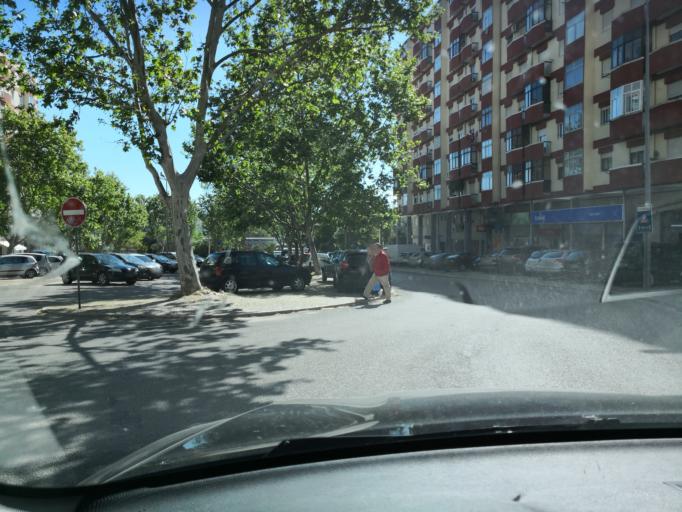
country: PT
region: Setubal
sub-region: Setubal
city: Setubal
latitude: 38.5372
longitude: -8.8925
